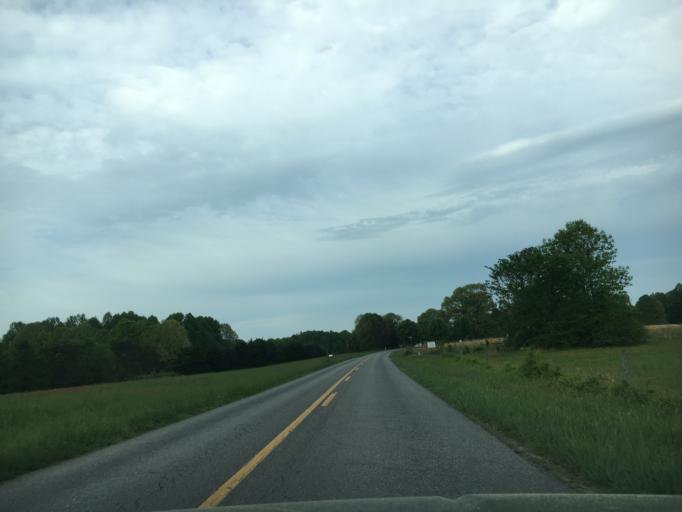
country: US
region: Virginia
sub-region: Halifax County
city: Halifax
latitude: 36.9088
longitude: -78.9195
